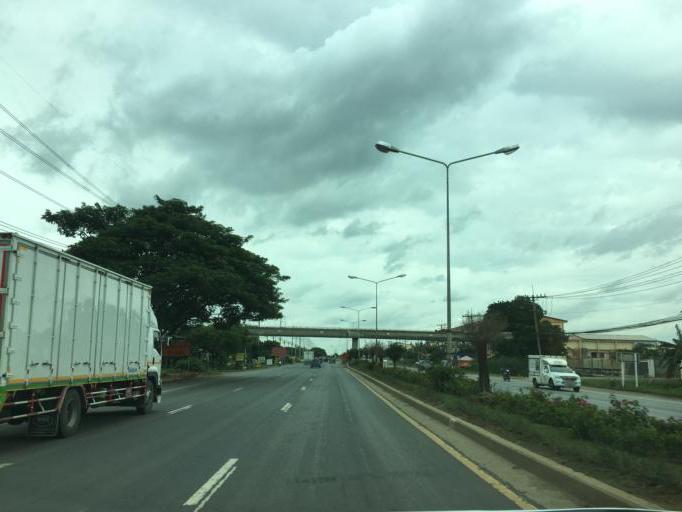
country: TH
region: Phra Nakhon Si Ayutthaya
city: Wang Noi
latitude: 14.2675
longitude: 100.6882
